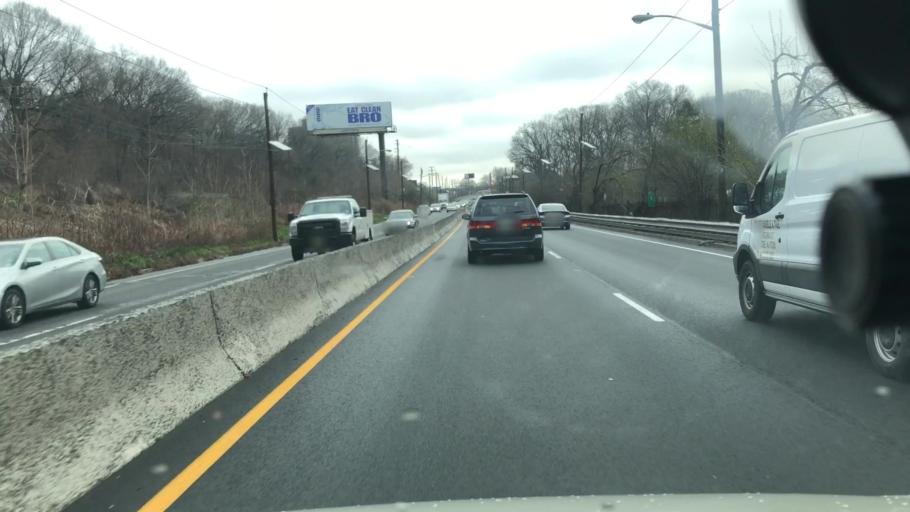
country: US
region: New Jersey
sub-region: Union County
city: Hillside
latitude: 40.7042
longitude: -74.2035
